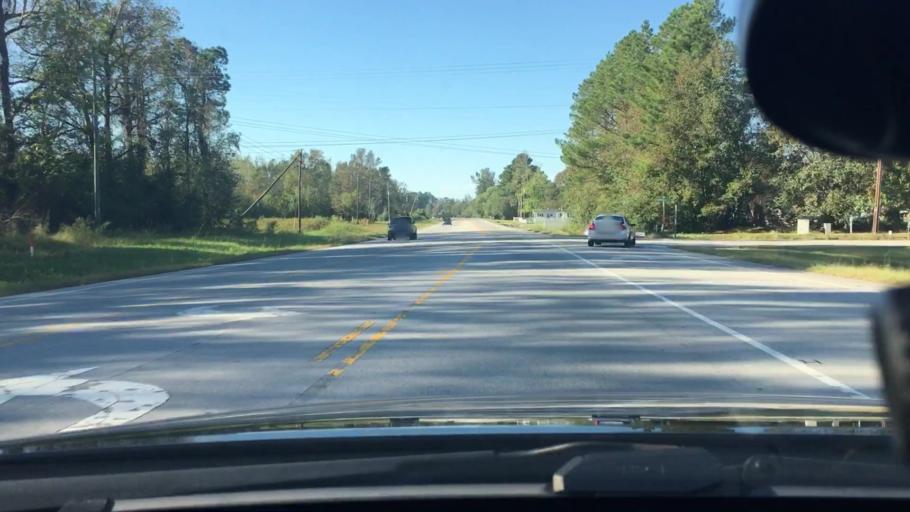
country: US
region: North Carolina
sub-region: Craven County
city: Trent Woods
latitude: 35.1551
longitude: -77.1124
